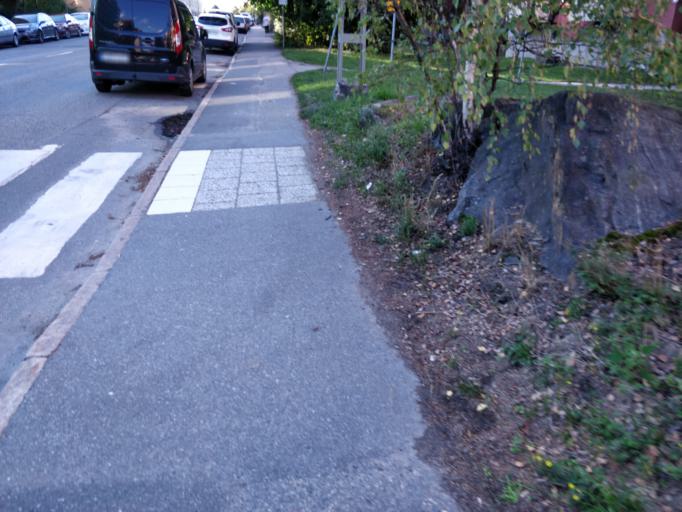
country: SE
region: Stockholm
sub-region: Stockholms Kommun
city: Arsta
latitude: 59.2955
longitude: 18.0552
